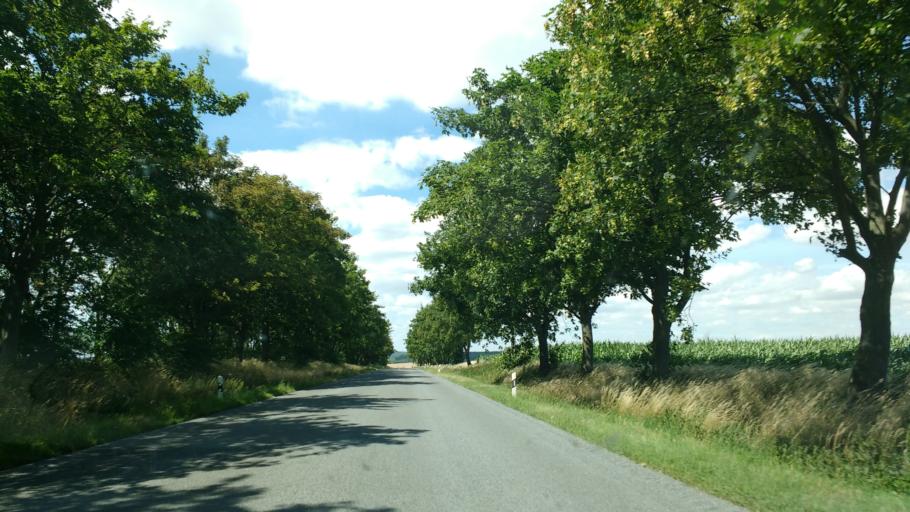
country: DE
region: Saxony-Anhalt
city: Farnstadt
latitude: 51.4174
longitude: 11.5740
